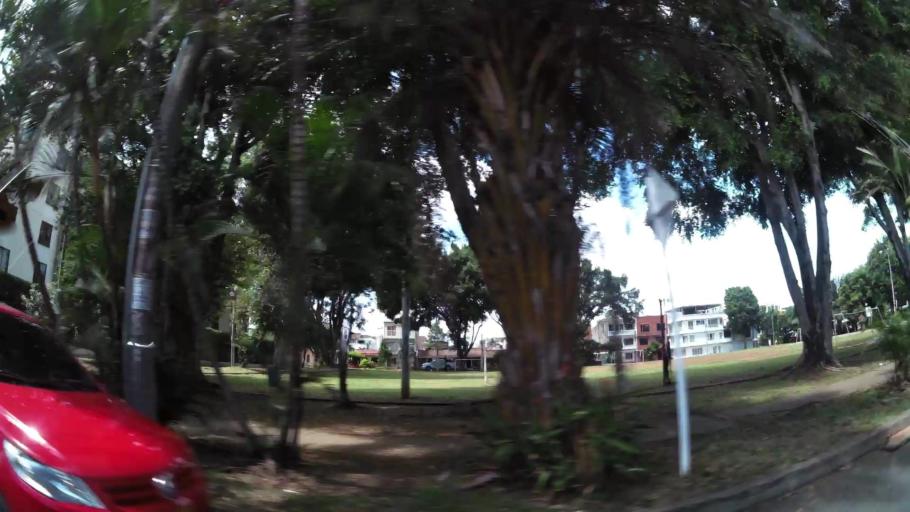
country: CO
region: Valle del Cauca
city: Cali
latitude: 3.3821
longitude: -76.5228
